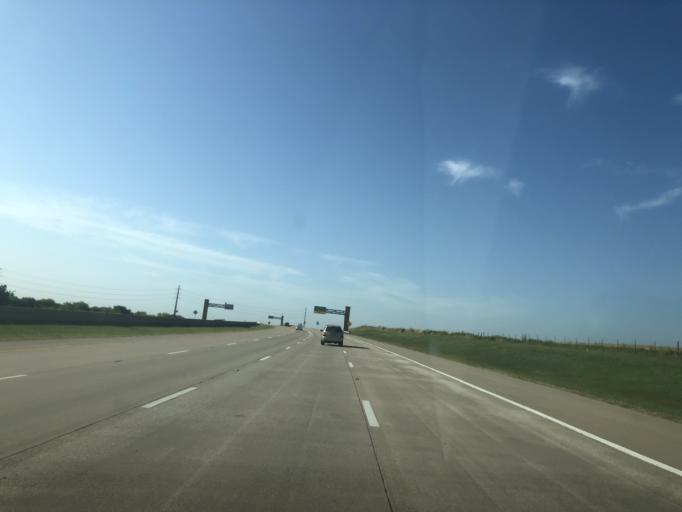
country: US
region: Texas
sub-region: Tarrant County
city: Benbrook
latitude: 32.6402
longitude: -97.4167
